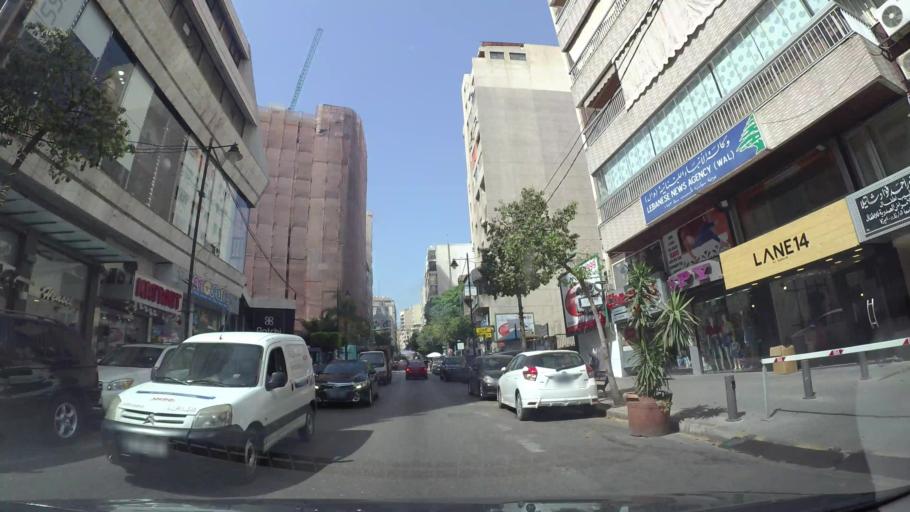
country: LB
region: Beyrouth
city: Beirut
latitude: 33.8847
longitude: 35.4924
